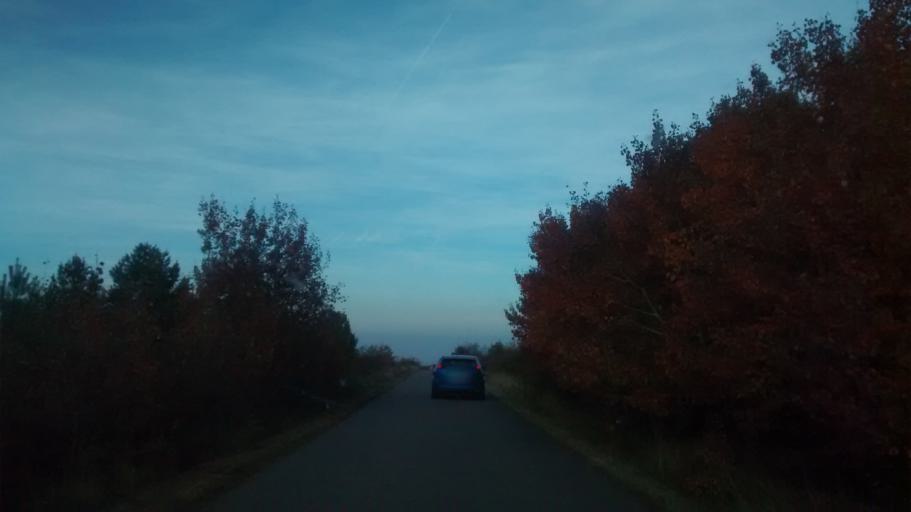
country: ES
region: Aragon
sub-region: Provincia de Zaragoza
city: Litago
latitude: 41.7909
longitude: -1.7664
